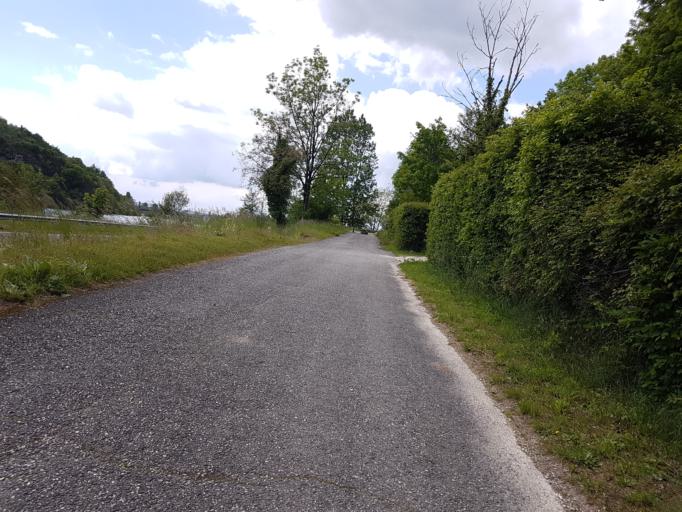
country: FR
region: Rhone-Alpes
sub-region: Departement de la Savoie
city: Saint-Genix-sur-Guiers
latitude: 45.6409
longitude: 5.6329
